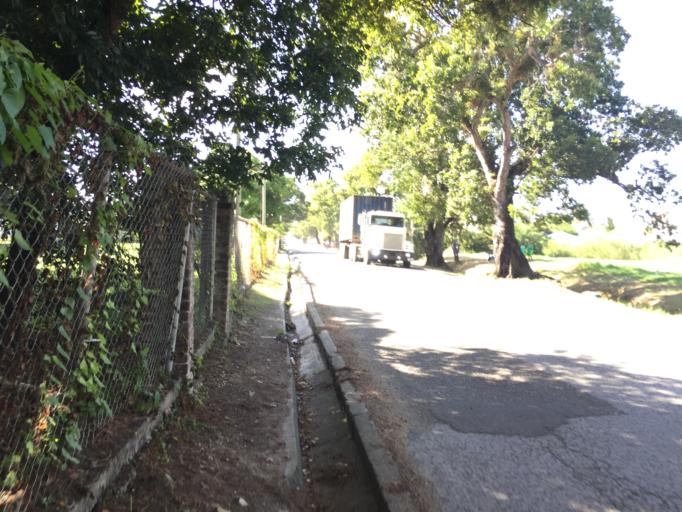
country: AG
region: Saint John
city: Saint John's
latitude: 17.1259
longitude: -61.8433
